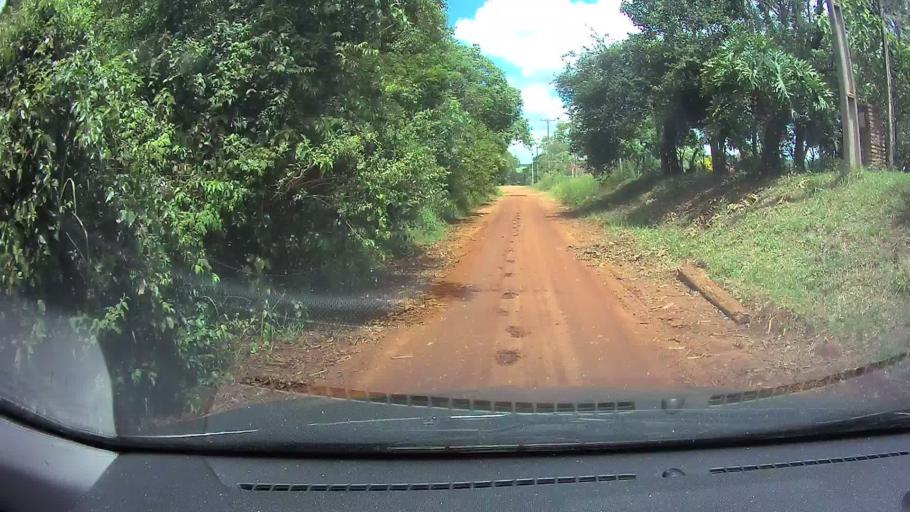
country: PY
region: Paraguari
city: La Colmena
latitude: -25.9491
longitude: -56.7822
